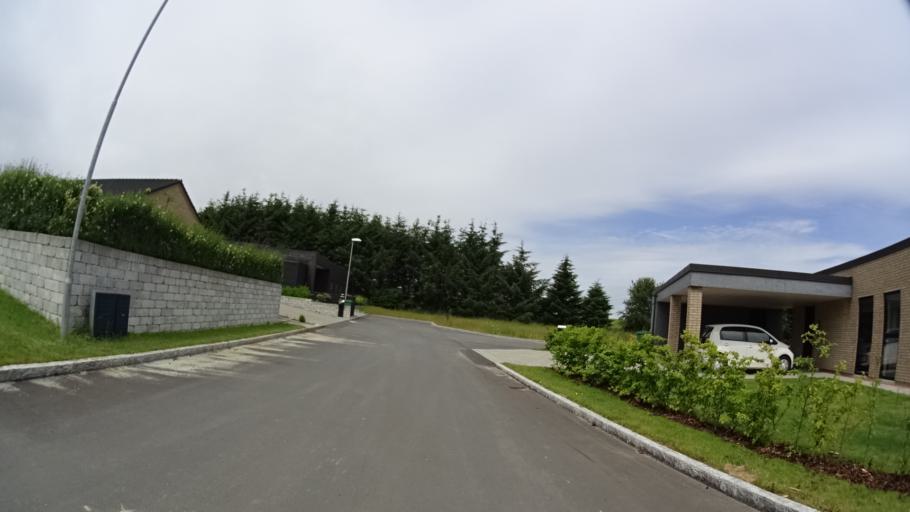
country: DK
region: Central Jutland
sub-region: Arhus Kommune
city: Stavtrup
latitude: 56.1218
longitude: 10.1222
